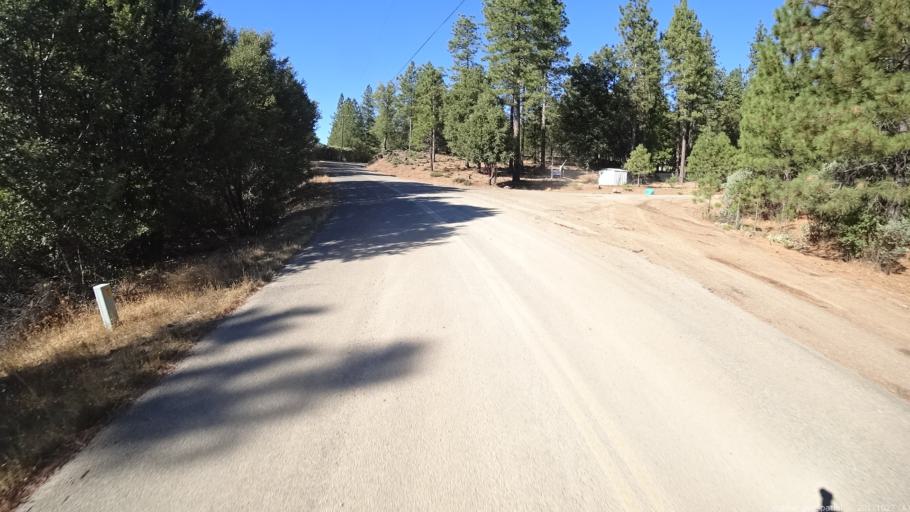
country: US
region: California
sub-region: Shasta County
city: Shingletown
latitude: 40.6618
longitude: -121.8823
